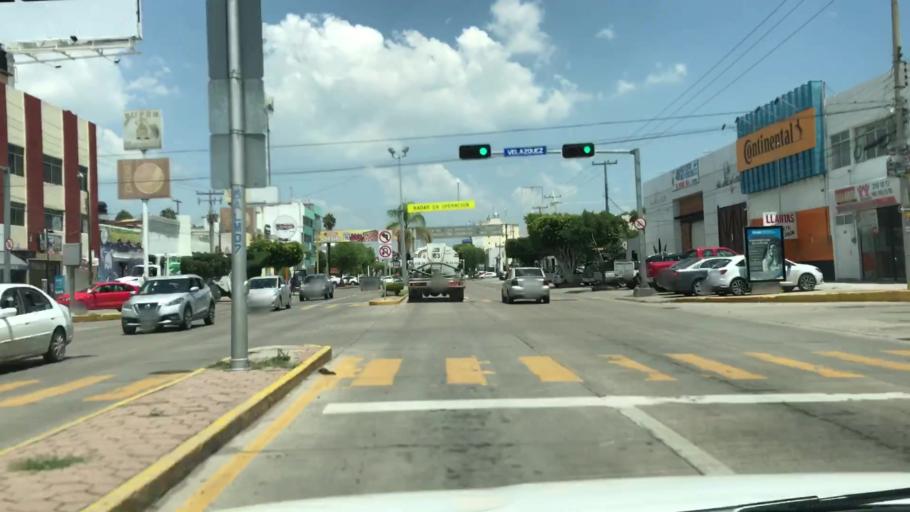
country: MX
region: Guanajuato
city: Celaya
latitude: 20.5190
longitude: -100.8342
